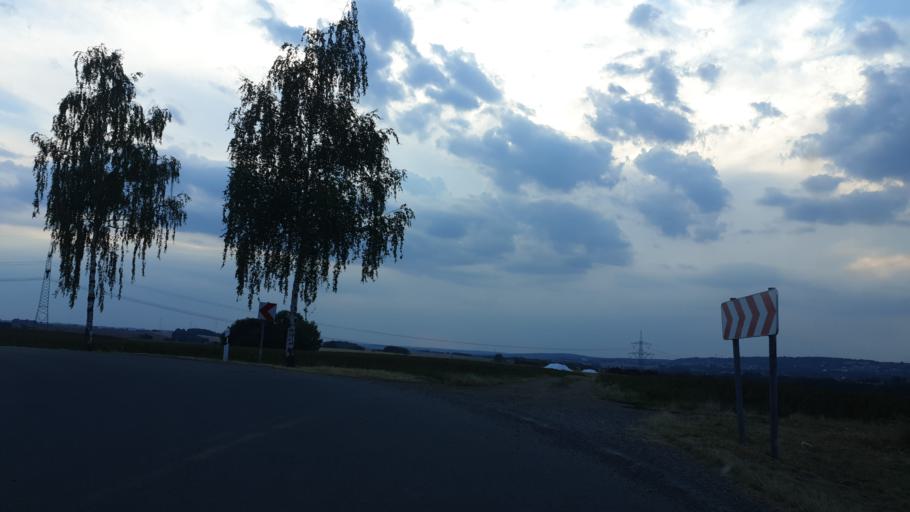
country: DE
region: Saxony
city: Niederdorf
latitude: 50.7826
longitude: 12.7921
